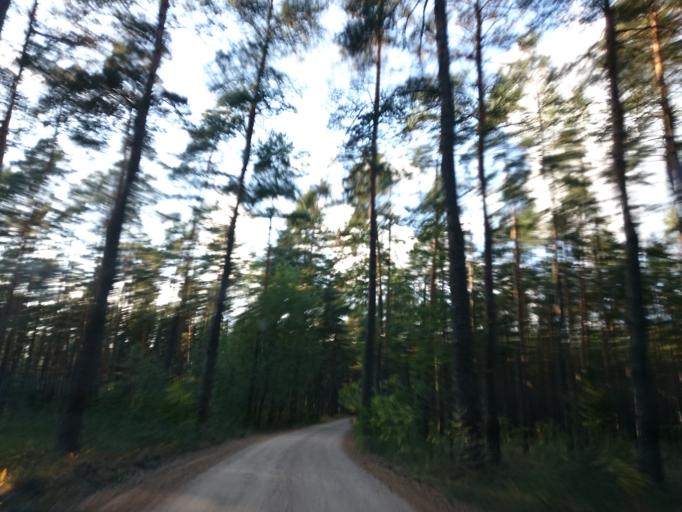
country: LV
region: Adazi
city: Adazi
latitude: 57.0552
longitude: 24.2998
